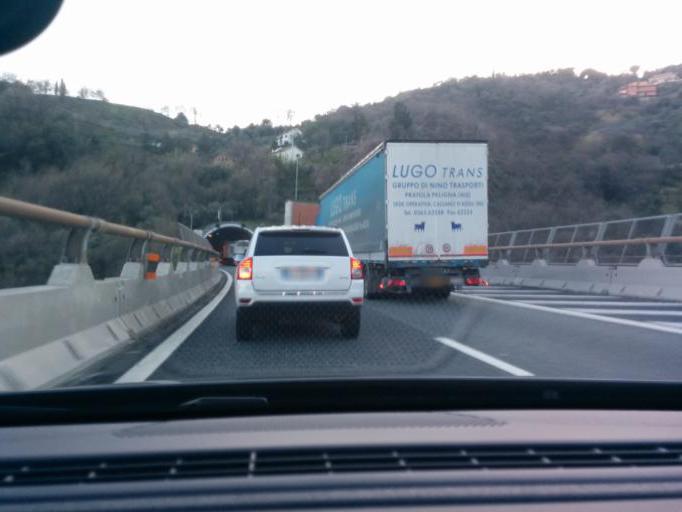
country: IT
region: Liguria
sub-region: Provincia di Savona
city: Varazze
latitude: 44.3672
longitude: 8.5714
